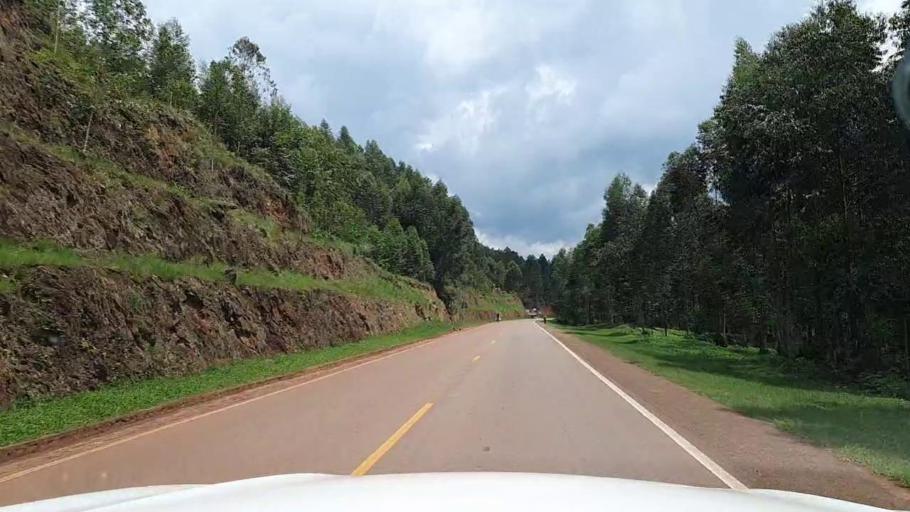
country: RW
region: Kigali
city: Kigali
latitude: -1.8143
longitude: 30.1191
